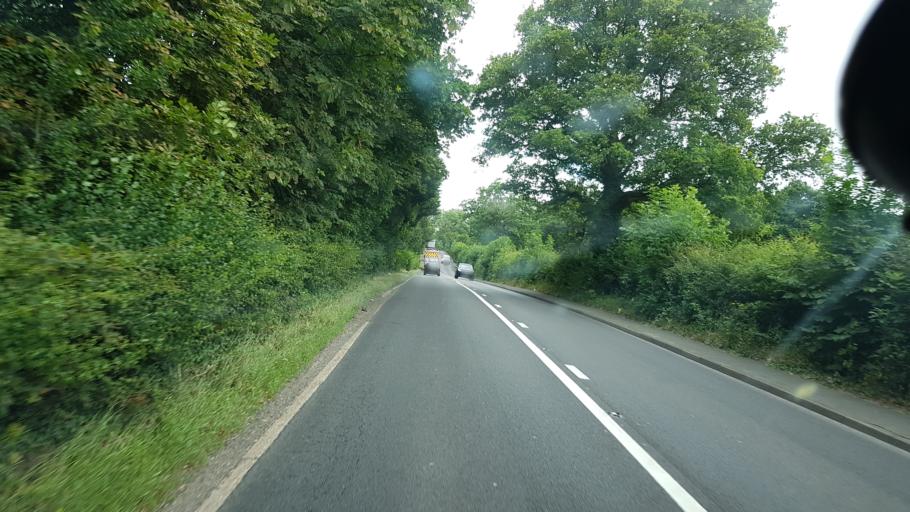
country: GB
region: England
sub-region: Surrey
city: Godstone
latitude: 51.2110
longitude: -0.0538
